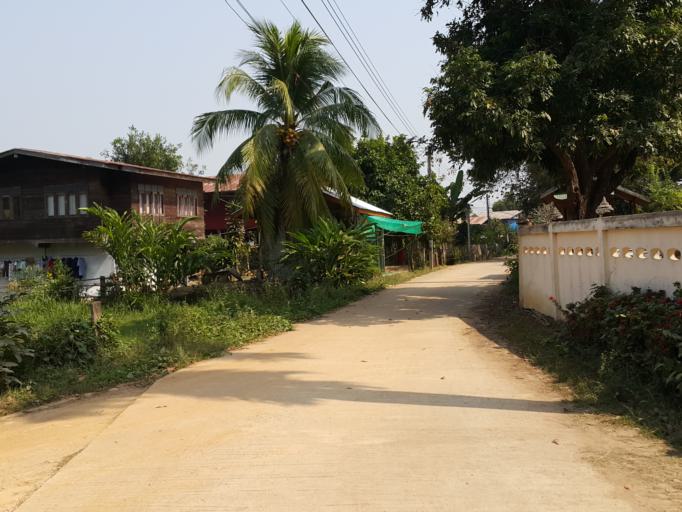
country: TH
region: Sukhothai
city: Thung Saliam
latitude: 17.3209
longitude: 99.5110
